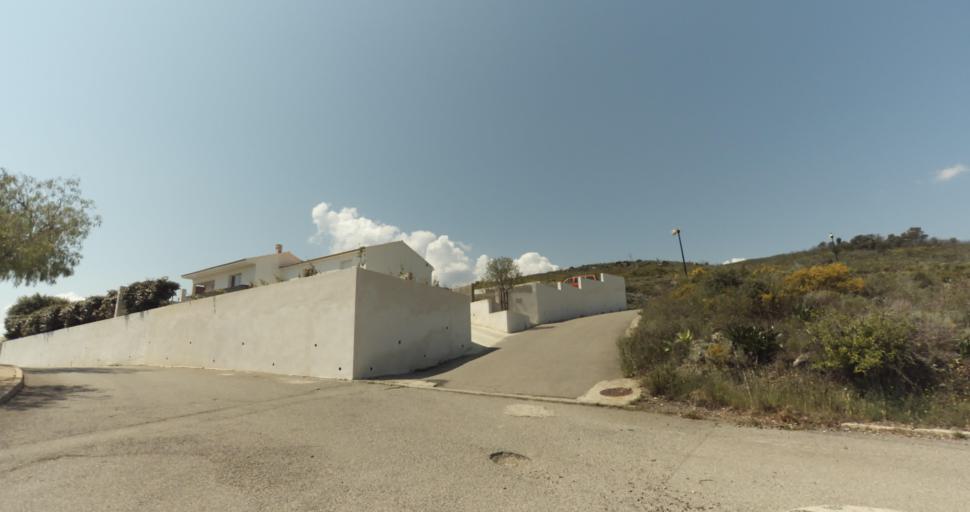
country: FR
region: Corsica
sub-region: Departement de la Haute-Corse
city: Biguglia
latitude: 42.6013
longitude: 9.4306
